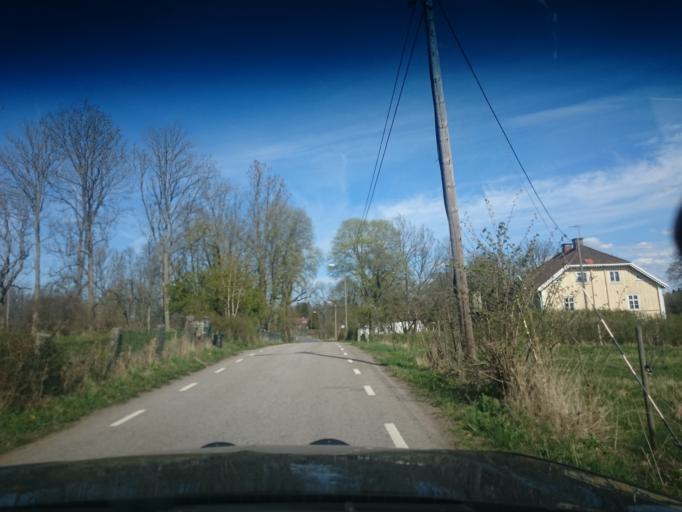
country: SE
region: Kronoberg
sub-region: Uppvidinge Kommun
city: Aseda
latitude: 57.3751
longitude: 15.3766
